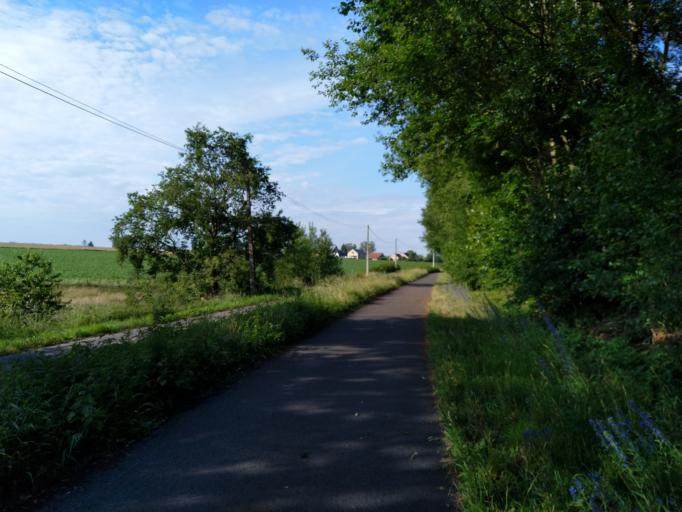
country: BE
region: Wallonia
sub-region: Province du Hainaut
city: Estinnes-au-Val
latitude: 50.3717
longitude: 4.1193
